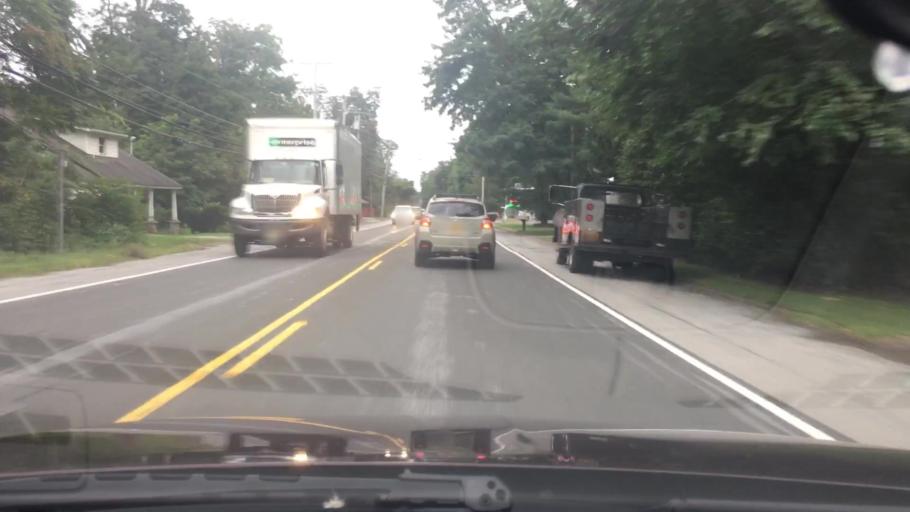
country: US
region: New York
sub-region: Dutchess County
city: Pleasant Valley
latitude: 41.7358
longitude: -73.8351
